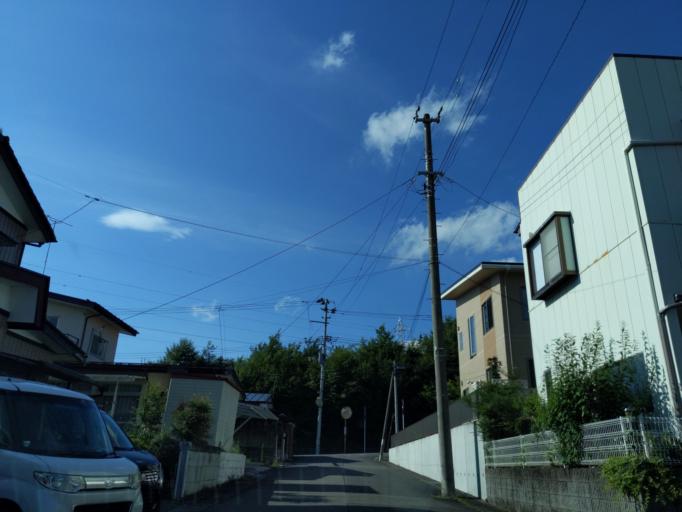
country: JP
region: Fukushima
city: Koriyama
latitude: 37.3975
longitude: 140.4199
